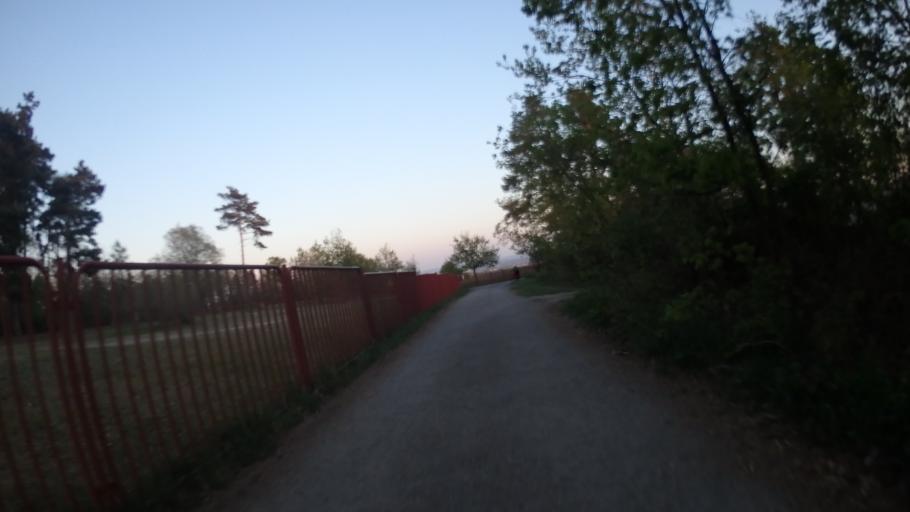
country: CZ
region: South Moravian
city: Ostopovice
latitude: 49.1819
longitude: 16.5538
